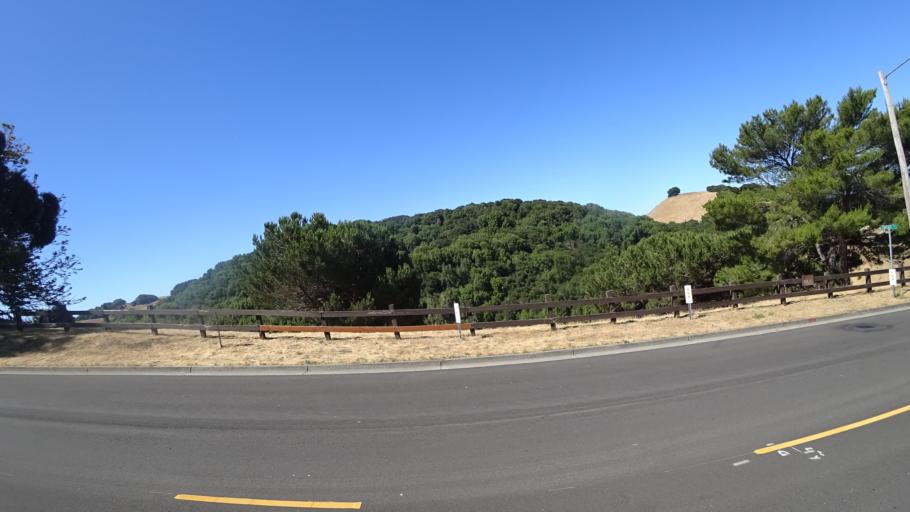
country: US
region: California
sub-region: Alameda County
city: Fairview
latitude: 37.6469
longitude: -122.0324
